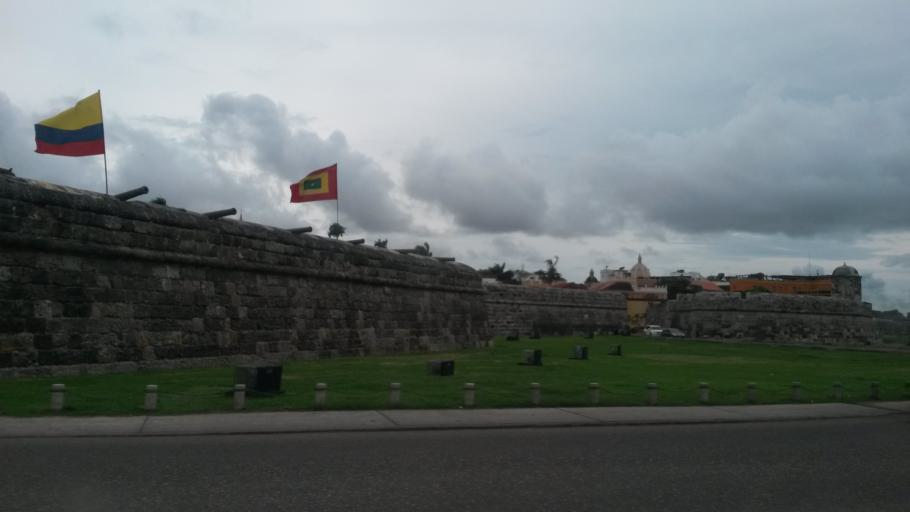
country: CO
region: Bolivar
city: Cartagena
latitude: 10.4244
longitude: -75.5545
